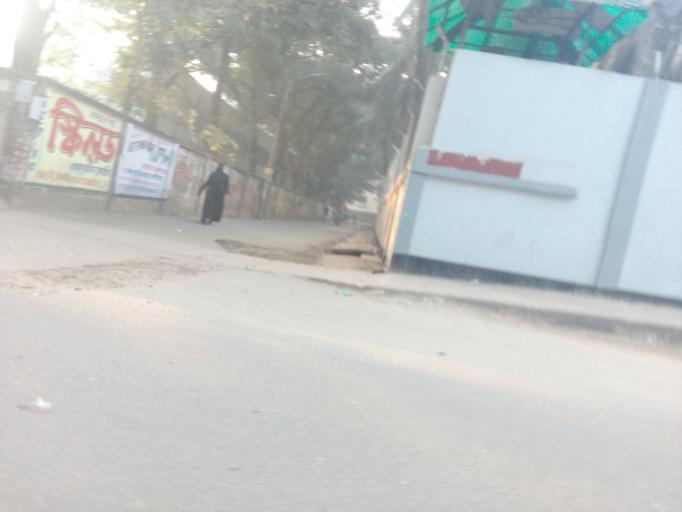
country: BD
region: Dhaka
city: Paltan
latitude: 23.7510
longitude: 90.4198
